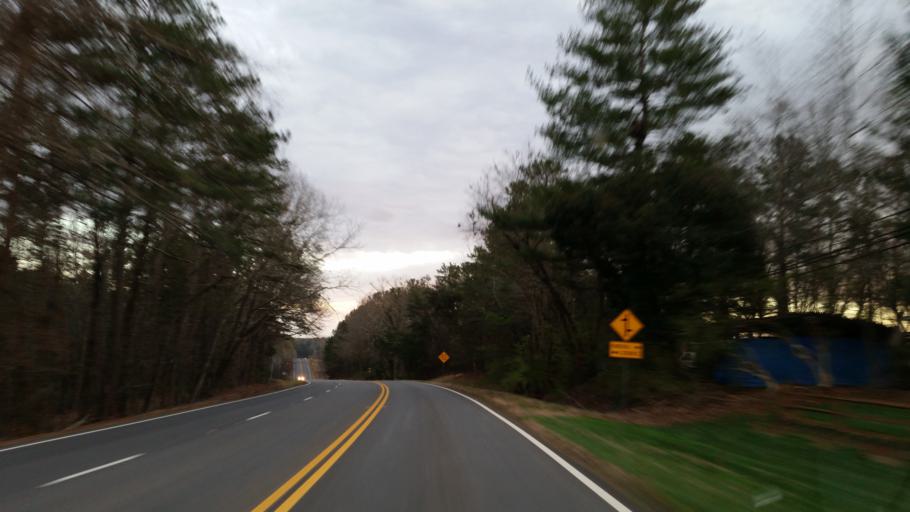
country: US
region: Georgia
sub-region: Pickens County
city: Nelson
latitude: 34.4251
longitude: -84.3957
